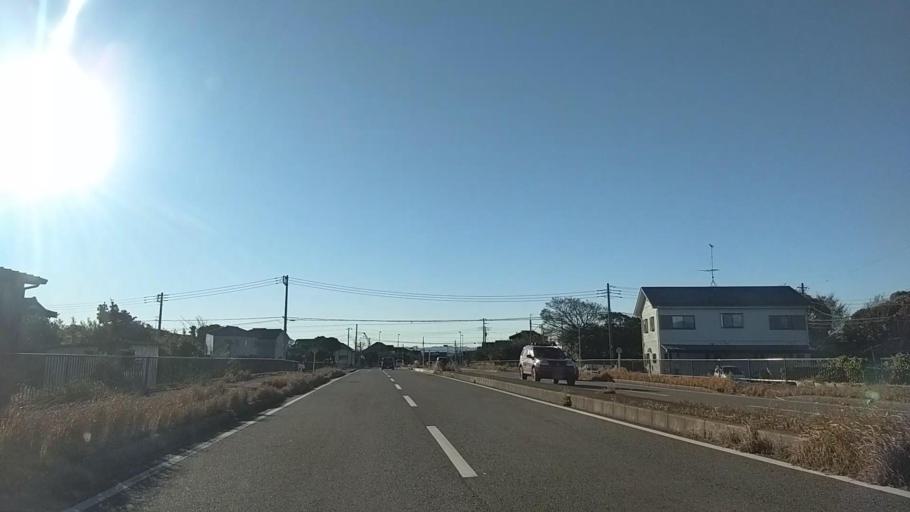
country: JP
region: Chiba
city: Kisarazu
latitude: 35.4012
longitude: 139.9203
